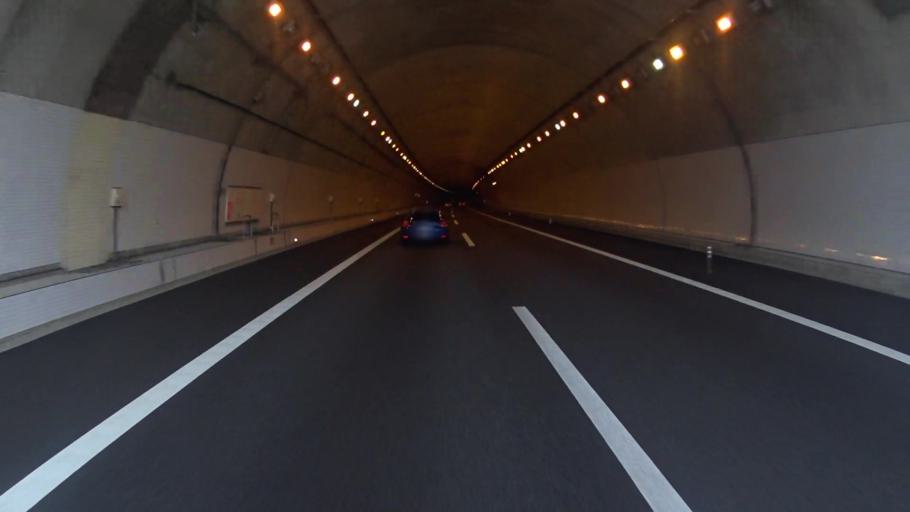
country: JP
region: Shiga Prefecture
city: Kusatsu
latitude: 34.9613
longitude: 135.9993
